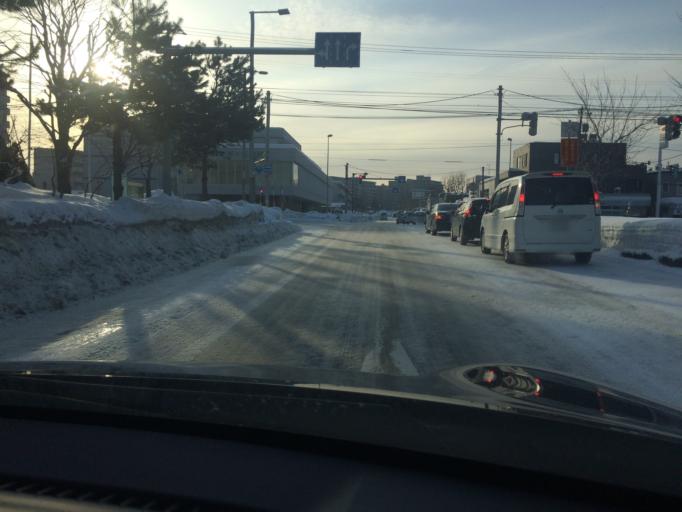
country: JP
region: Hokkaido
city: Ebetsu
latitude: 43.0361
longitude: 141.4742
